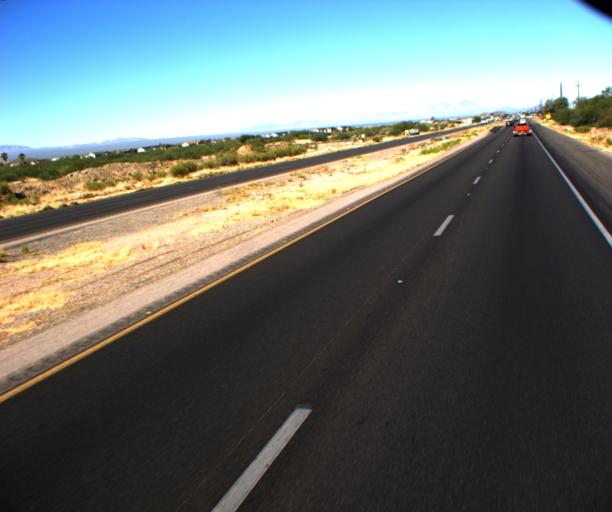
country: US
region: Arizona
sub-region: Pima County
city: Tucson Estates
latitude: 32.1733
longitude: -111.0648
